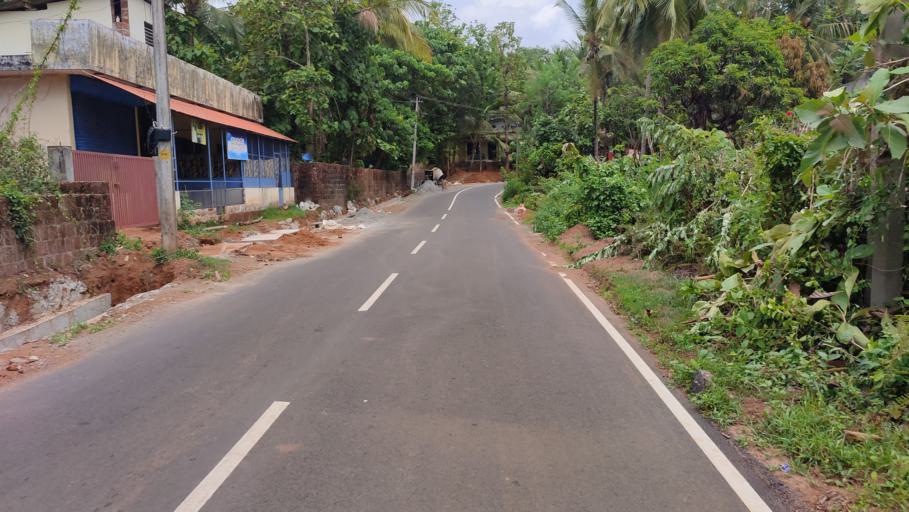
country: IN
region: Kerala
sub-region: Kasaragod District
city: Kannangad
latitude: 12.3198
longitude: 75.1139
